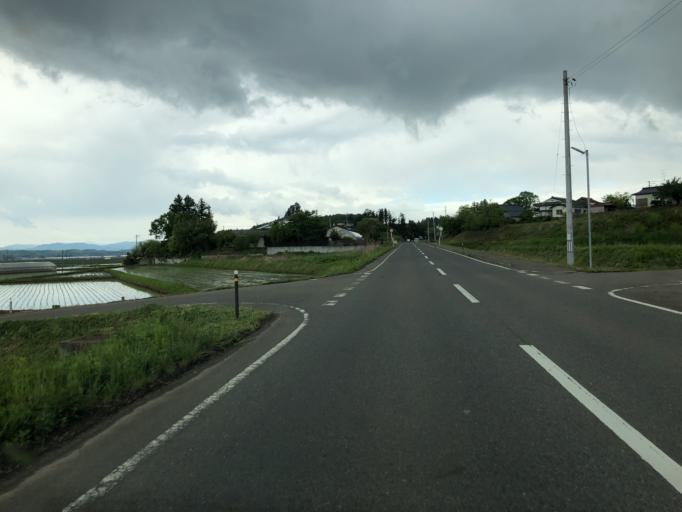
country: JP
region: Fukushima
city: Ishikawa
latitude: 37.1530
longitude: 140.3699
